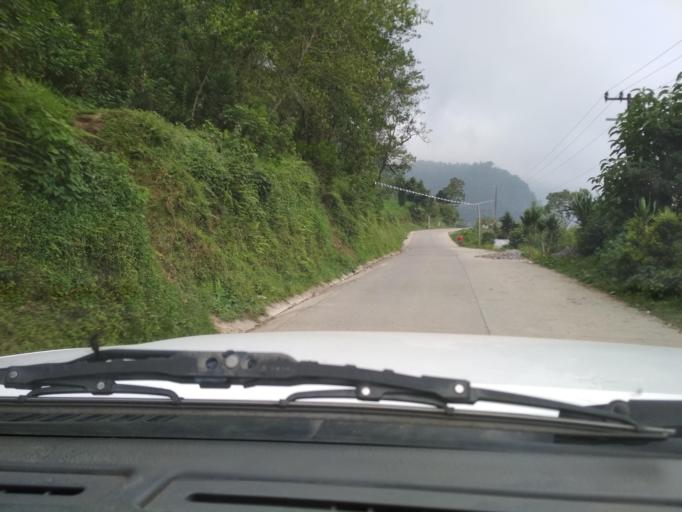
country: MX
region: Veracruz
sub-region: La Perla
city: Metlac Hernandez (Metlac Primero)
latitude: 18.9782
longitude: -97.1370
